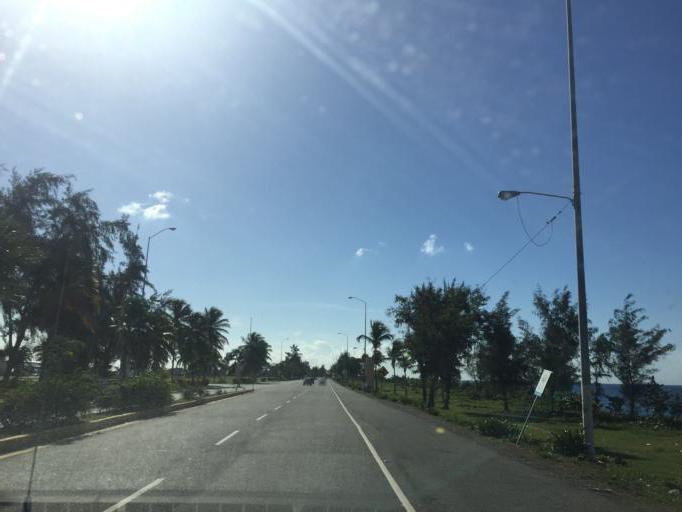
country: DO
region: Santo Domingo
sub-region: Santo Domingo
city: Boca Chica
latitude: 18.4366
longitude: -69.6813
